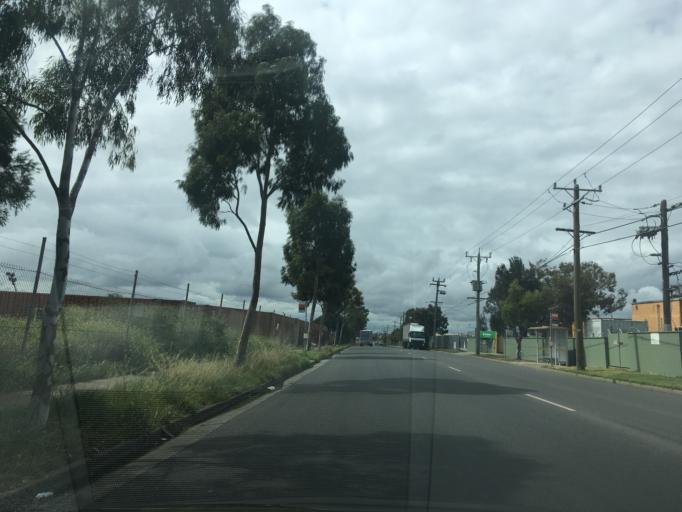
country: AU
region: Victoria
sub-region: Hobsons Bay
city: Laverton
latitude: -37.8359
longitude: 144.7992
